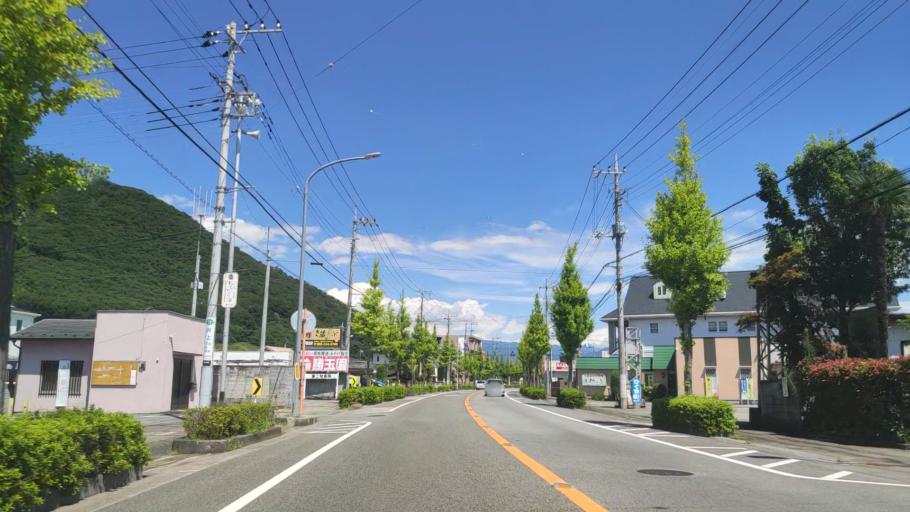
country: JP
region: Yamanashi
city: Isawa
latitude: 35.6592
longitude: 138.6191
